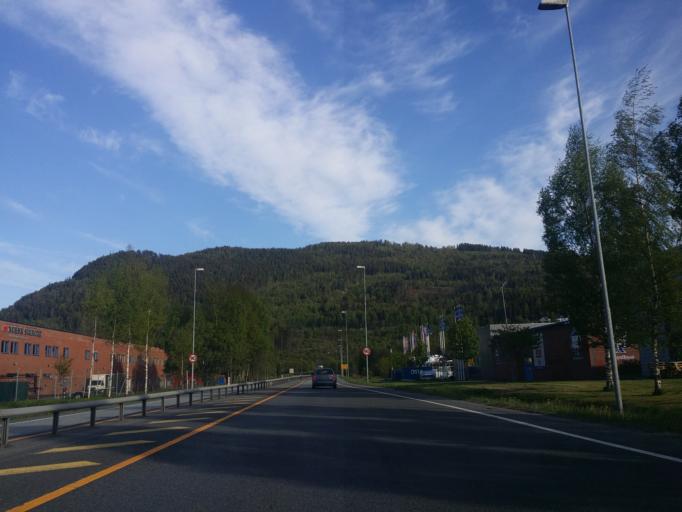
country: NO
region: Buskerud
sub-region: Nedre Eiker
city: Mjondalen
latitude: 59.7502
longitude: 10.0305
